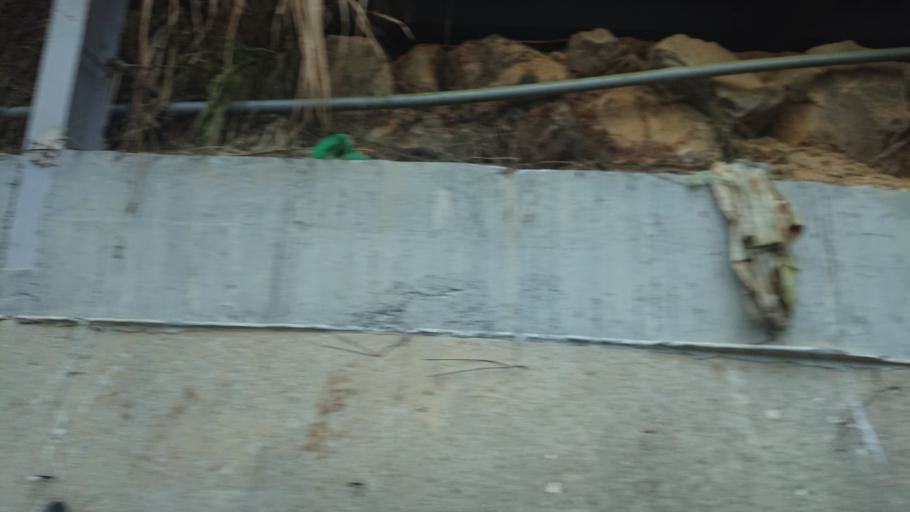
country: TW
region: Taiwan
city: Lugu
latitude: 23.6184
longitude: 120.7207
